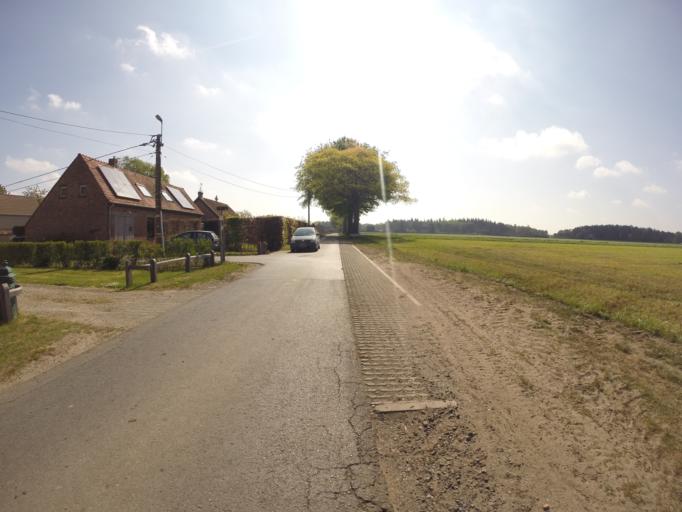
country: BE
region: Flanders
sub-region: Provincie West-Vlaanderen
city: Beernem
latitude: 51.0890
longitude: 3.3544
